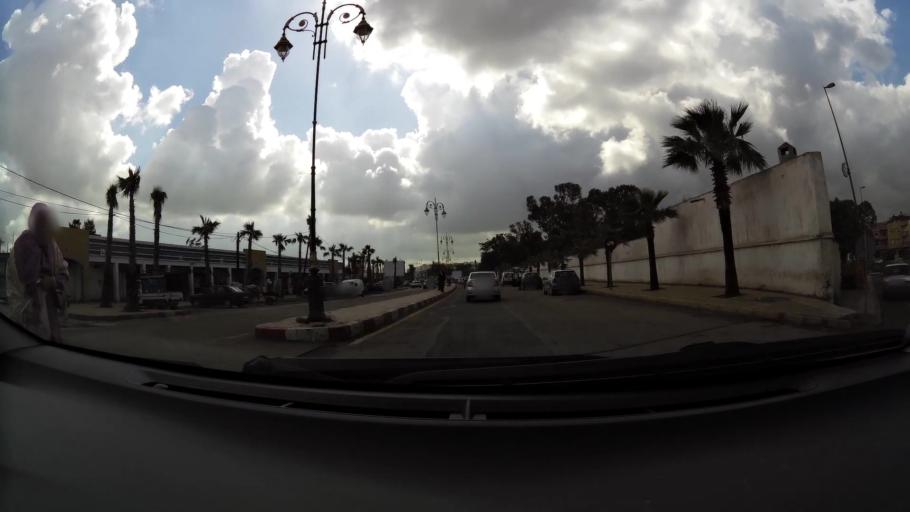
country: MA
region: Grand Casablanca
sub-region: Mediouna
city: Tit Mellil
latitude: 33.5556
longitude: -7.4824
